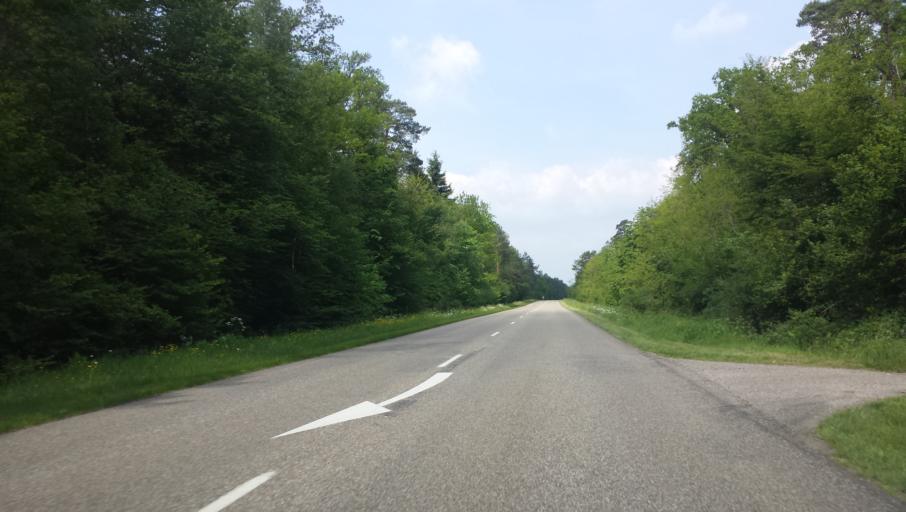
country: DE
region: Rheinland-Pfalz
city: Steinfeld
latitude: 49.0097
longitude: 8.0438
